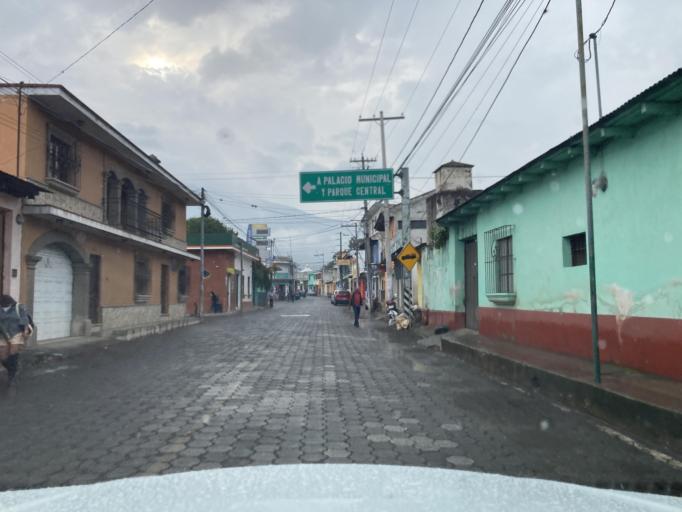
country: GT
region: Sacatepequez
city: San Miguel Duenas
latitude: 14.5246
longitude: -90.7966
